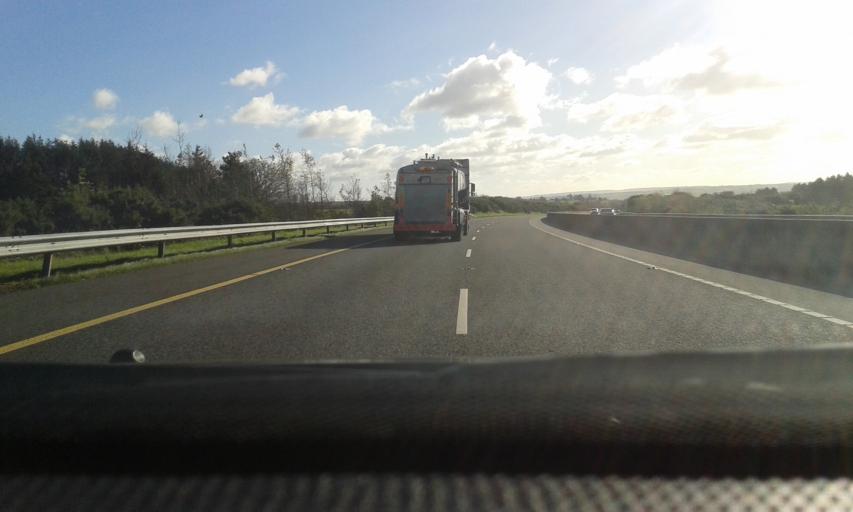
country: IE
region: Munster
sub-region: County Cork
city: Mitchelstown
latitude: 52.2148
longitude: -8.2789
